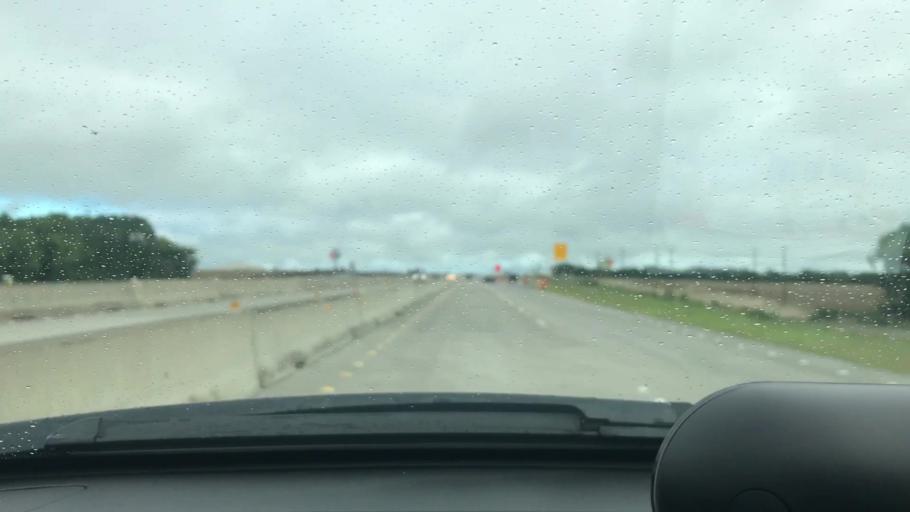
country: US
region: Texas
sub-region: Collin County
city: Anna
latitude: 33.3369
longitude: -96.5879
